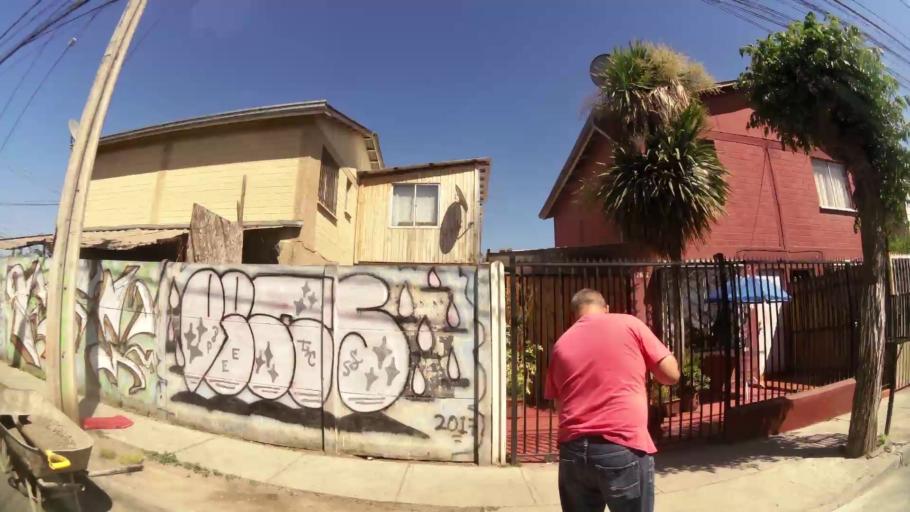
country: CL
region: Santiago Metropolitan
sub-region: Provincia de Maipo
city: San Bernardo
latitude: -33.6241
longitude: -70.6956
